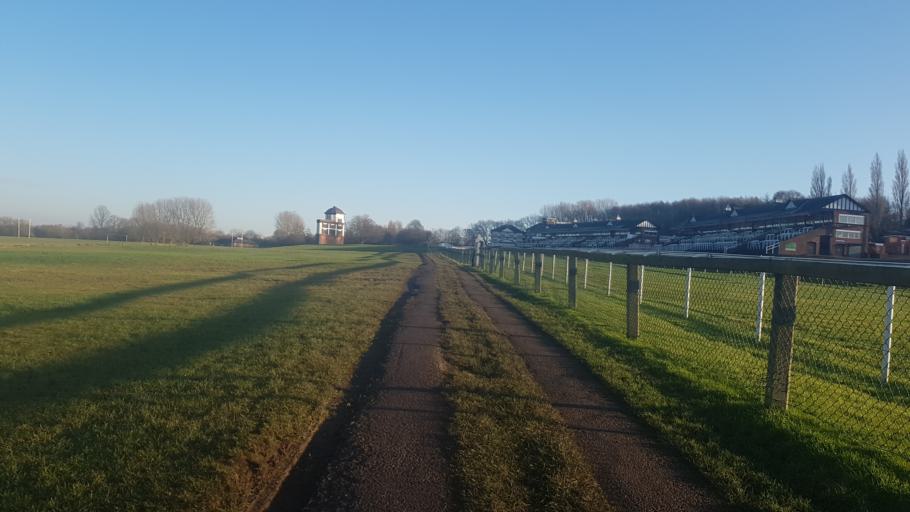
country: GB
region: England
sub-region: City and Borough of Wakefield
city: Pontefract
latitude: 53.6973
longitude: -1.3347
